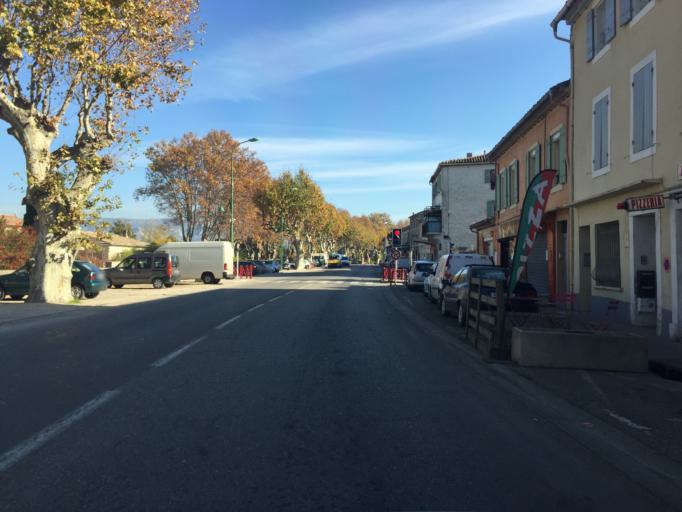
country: FR
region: Provence-Alpes-Cote d'Azur
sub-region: Departement des Bouches-du-Rhone
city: Orgon
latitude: 43.7921
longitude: 5.0387
